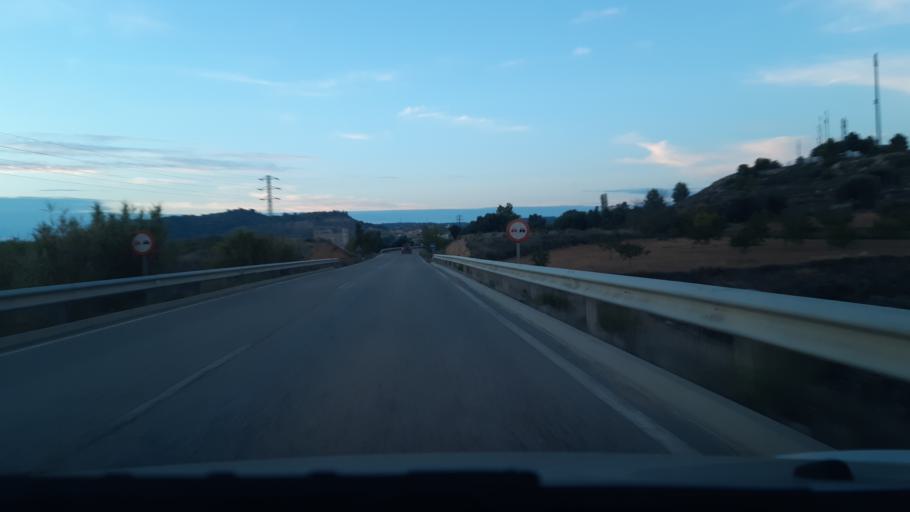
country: ES
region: Aragon
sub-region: Provincia de Teruel
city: Valderrobres
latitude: 40.8675
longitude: 0.1622
